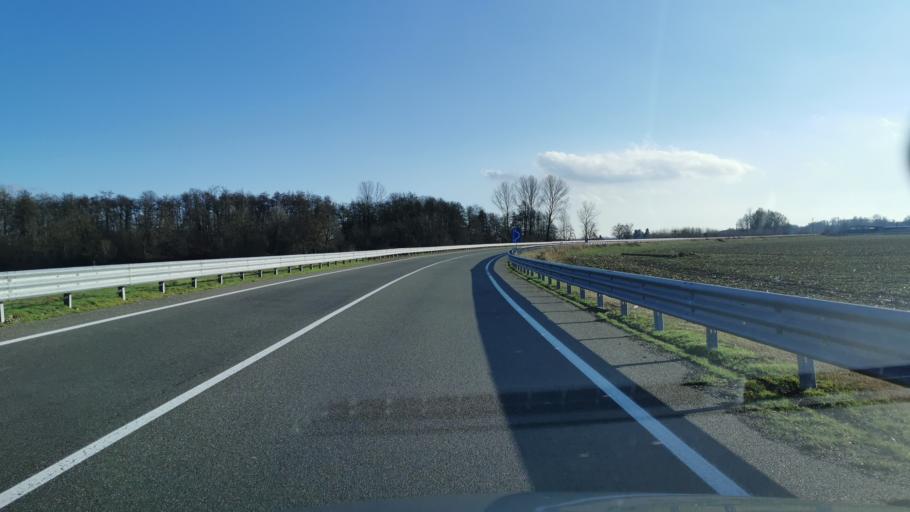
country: IT
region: Piedmont
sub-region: Provincia di Biella
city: Mottalciata
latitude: 45.5157
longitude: 8.2100
